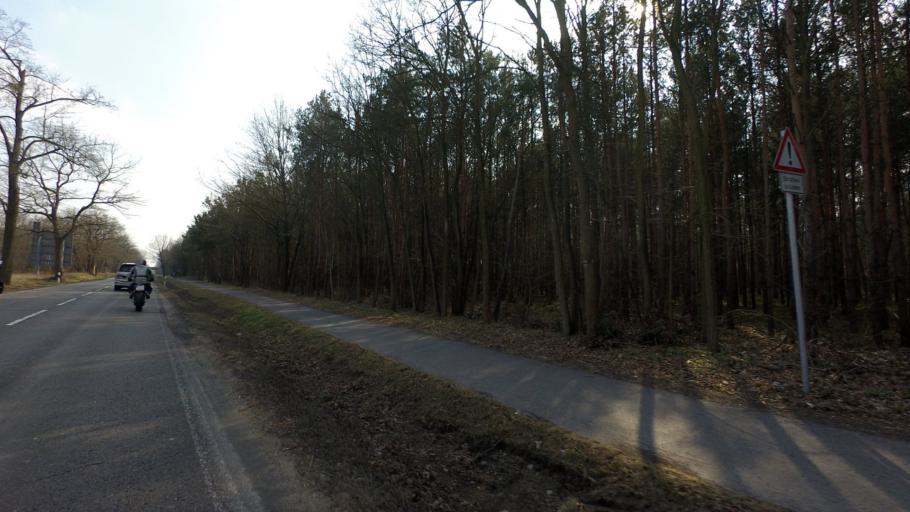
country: DE
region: Brandenburg
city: Potsdam
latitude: 52.3296
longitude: 13.1156
